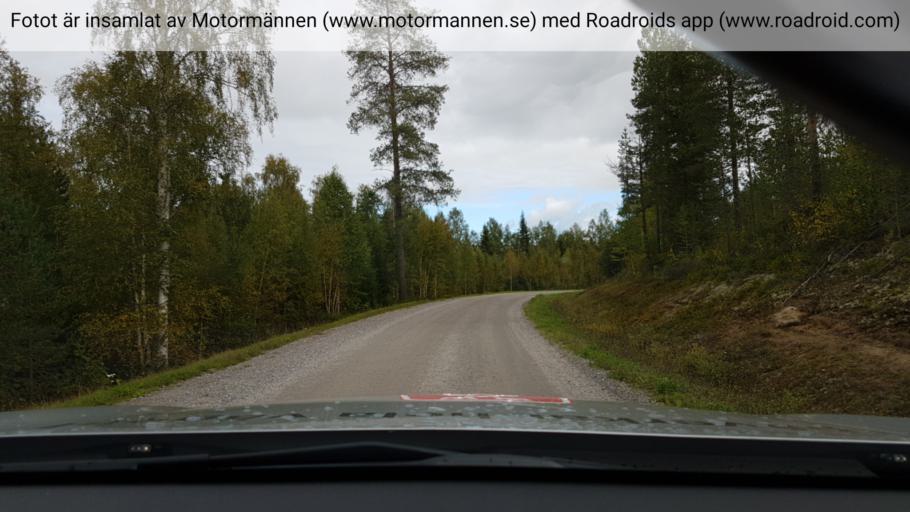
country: SE
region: Vaesterbotten
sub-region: Skelleftea Kommun
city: Byske
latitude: 65.1089
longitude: 21.1855
